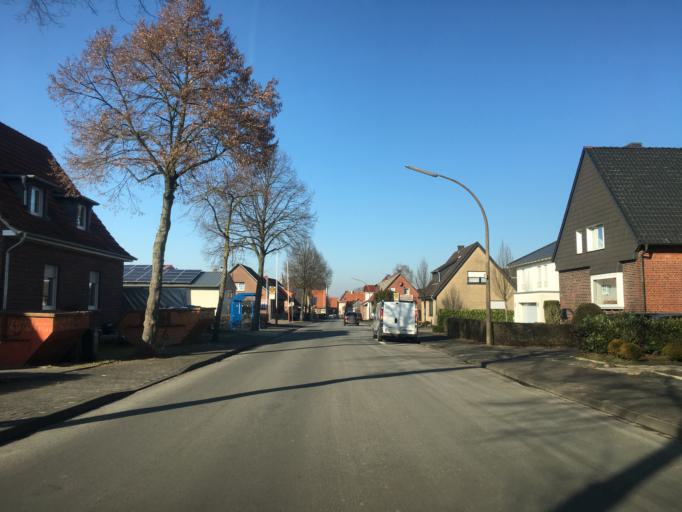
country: DE
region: North Rhine-Westphalia
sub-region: Regierungsbezirk Munster
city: Billerbeck
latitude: 52.0220
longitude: 7.2746
